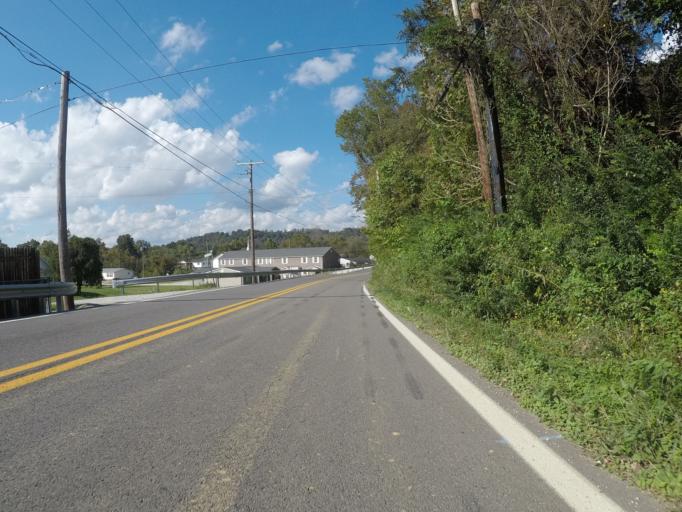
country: US
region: Ohio
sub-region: Lawrence County
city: Burlington
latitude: 38.3629
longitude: -82.5154
